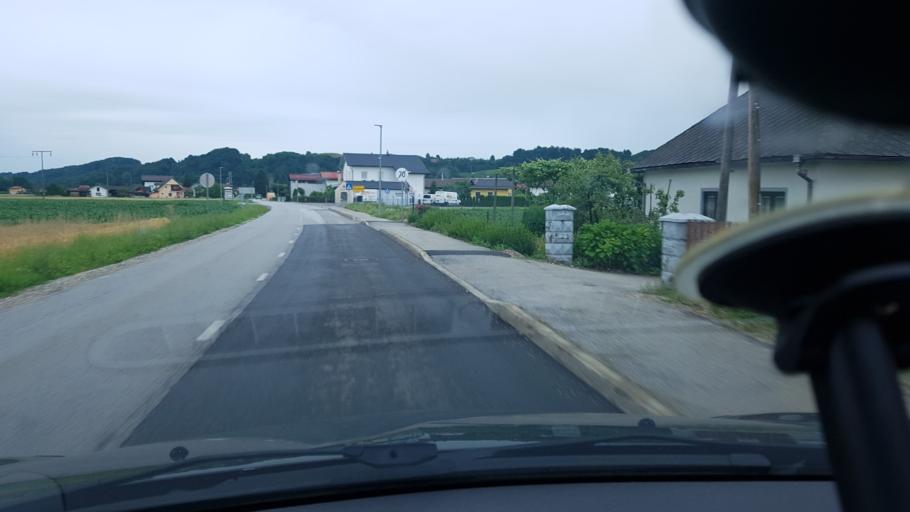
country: SI
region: Videm
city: Videm pri Ptuju
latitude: 46.3734
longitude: 15.8907
